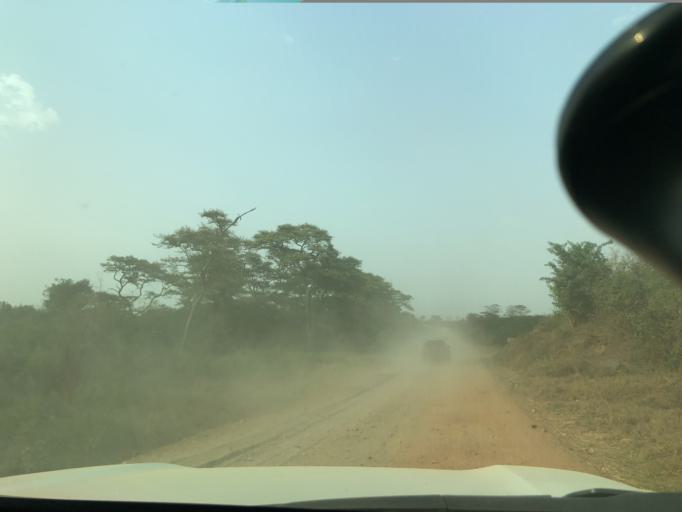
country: CD
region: Nord Kivu
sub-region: North Kivu
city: Butembo
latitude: 0.1400
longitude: 29.6435
